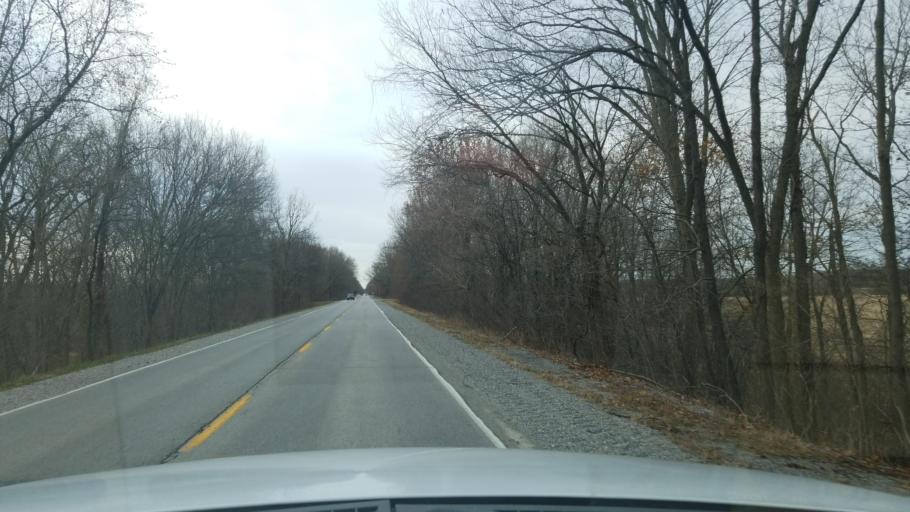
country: US
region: Illinois
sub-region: White County
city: Carmi
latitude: 37.9257
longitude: -88.1012
